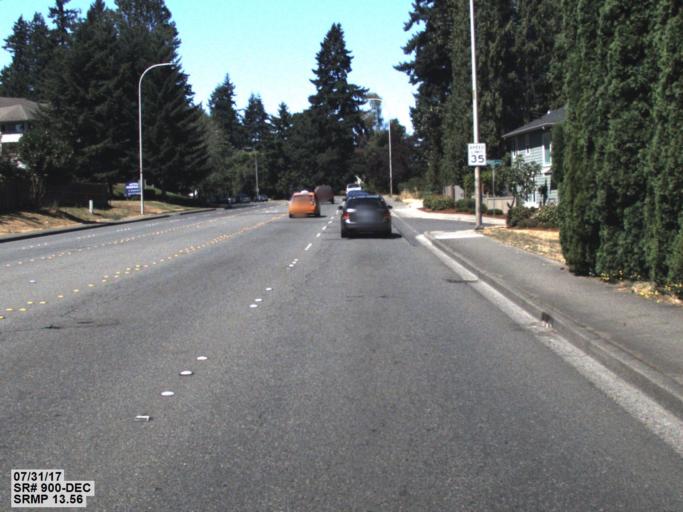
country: US
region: Washington
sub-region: King County
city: Newcastle
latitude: 47.5059
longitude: -122.1711
